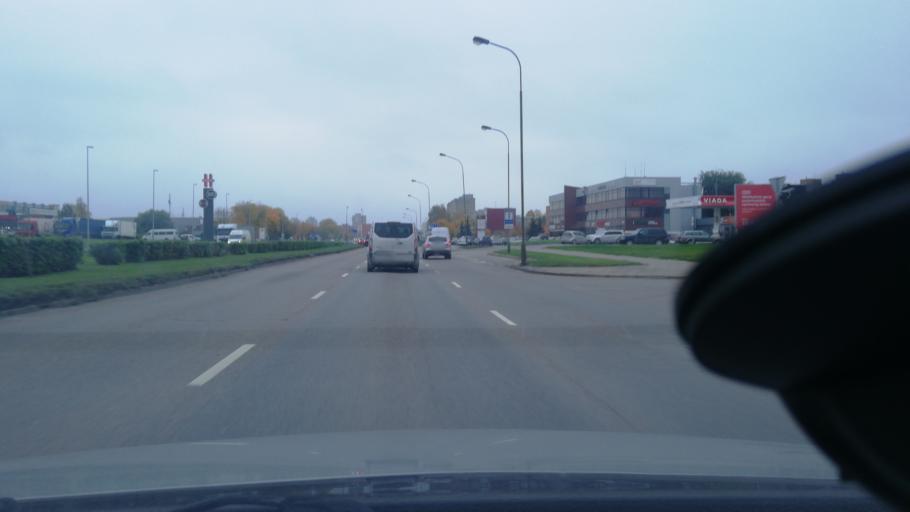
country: LT
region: Klaipedos apskritis
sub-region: Klaipeda
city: Klaipeda
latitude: 55.6826
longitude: 21.1854
